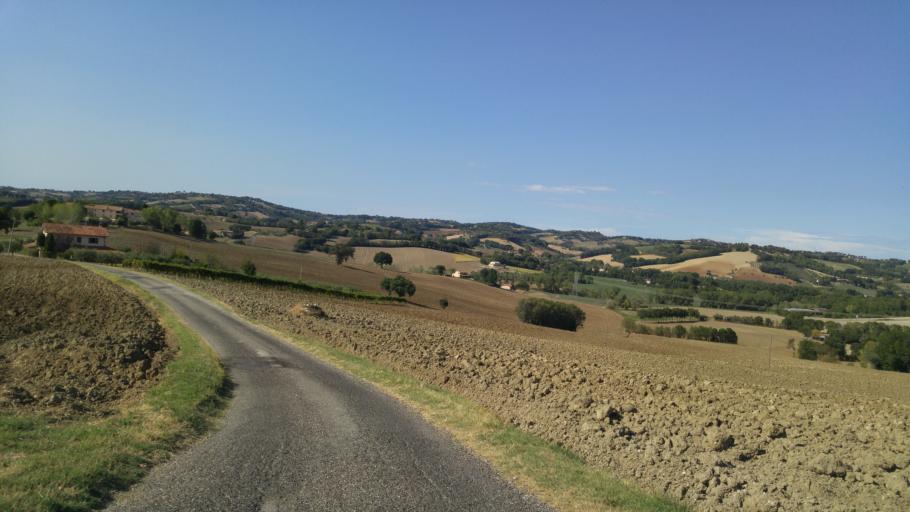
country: IT
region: The Marches
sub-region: Provincia di Pesaro e Urbino
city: Lucrezia
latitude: 43.8186
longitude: 12.9106
